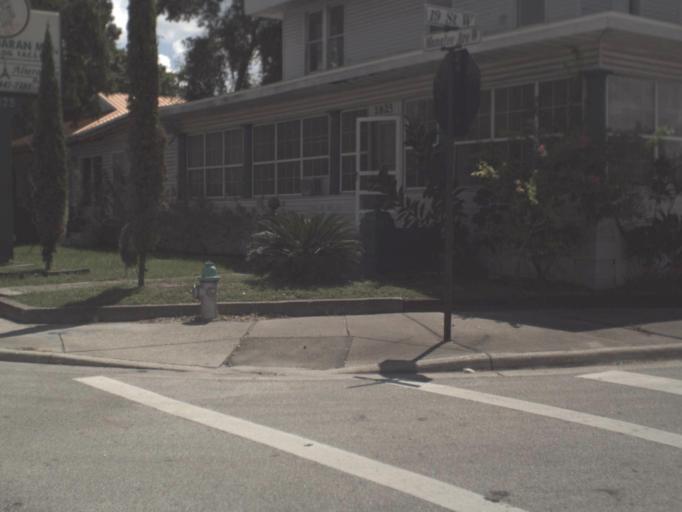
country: US
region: Florida
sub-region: Manatee County
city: Bradenton
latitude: 27.4955
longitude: -82.5805
